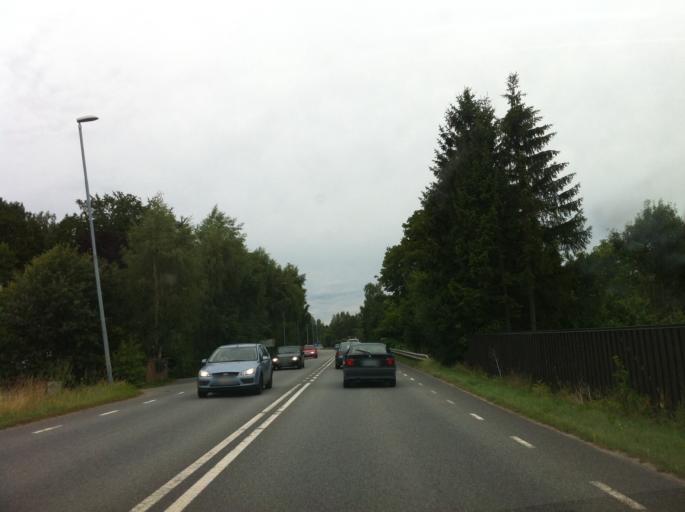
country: SE
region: Skane
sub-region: Hoors Kommun
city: Hoeoer
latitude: 55.9501
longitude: 13.5597
